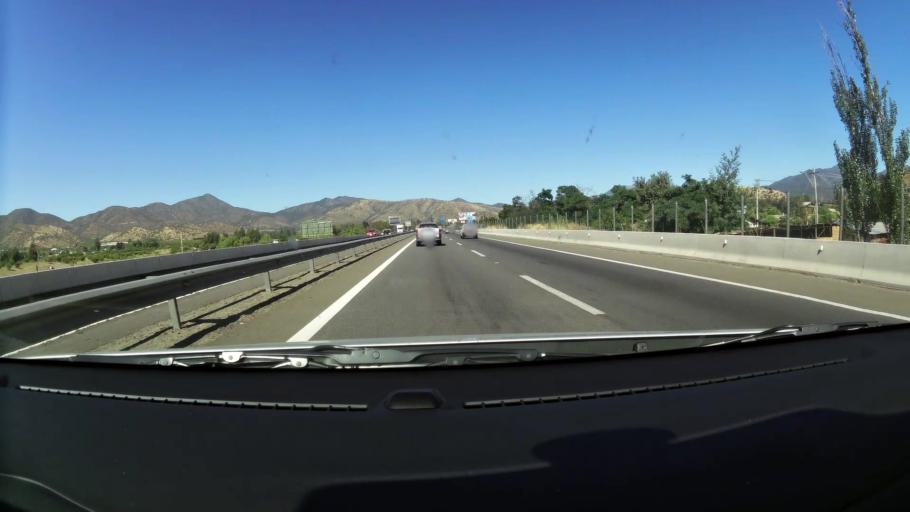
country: CL
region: Santiago Metropolitan
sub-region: Provincia de Melipilla
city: Melipilla
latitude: -33.4110
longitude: -71.1439
